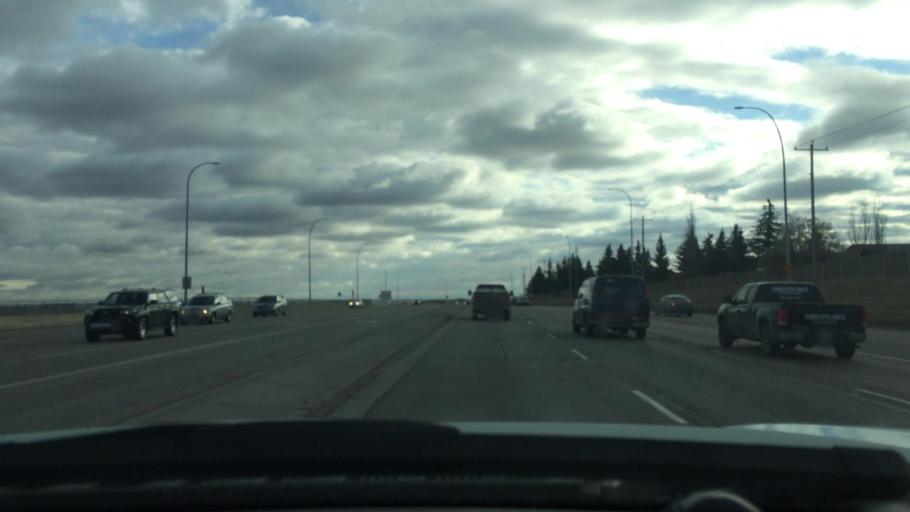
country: CA
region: Alberta
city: Calgary
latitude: 51.1379
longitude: -114.0807
